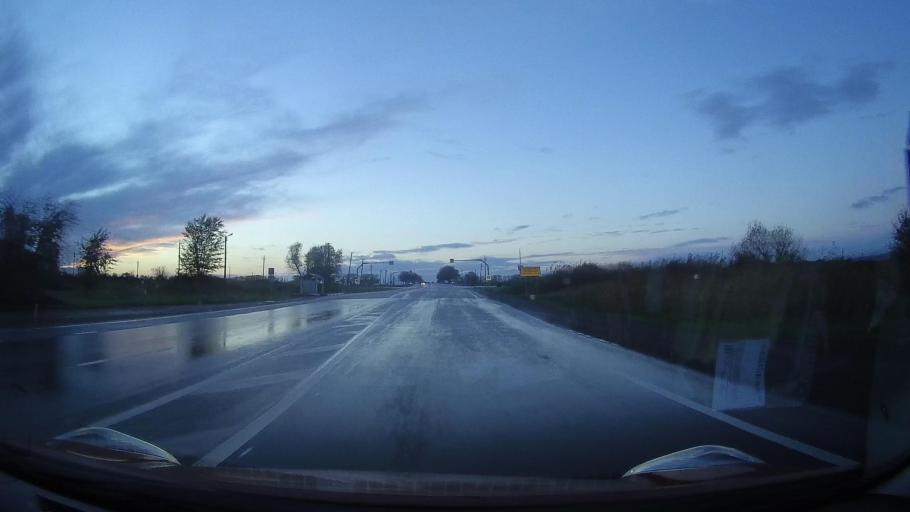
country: RU
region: Krasnodarskiy
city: Konokovo
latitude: 44.8290
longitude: 41.3427
